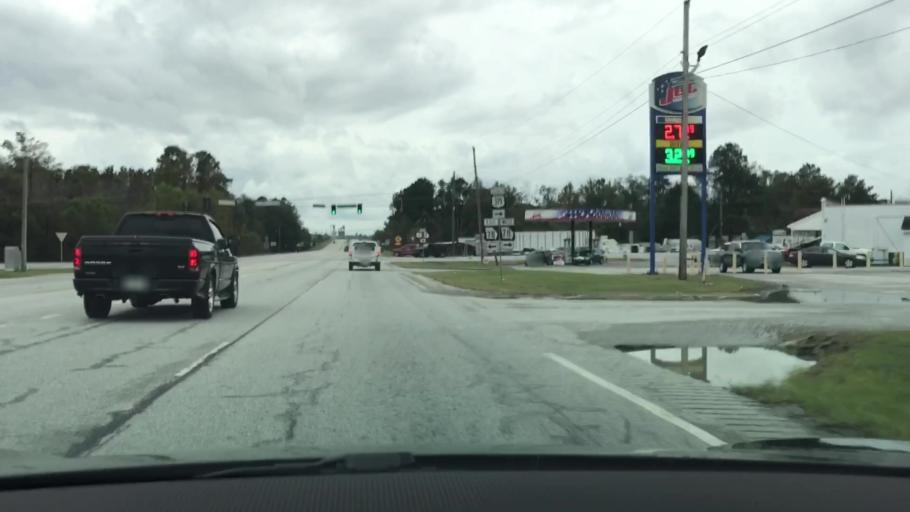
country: US
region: Georgia
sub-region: Jefferson County
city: Wadley
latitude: 32.8685
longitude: -82.3954
